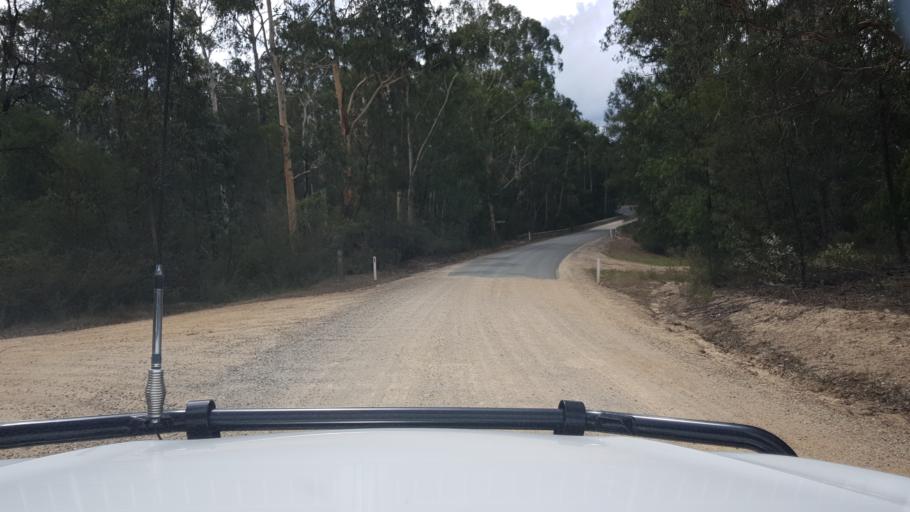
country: AU
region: Victoria
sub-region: East Gippsland
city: Bairnsdale
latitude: -37.6793
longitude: 147.5512
